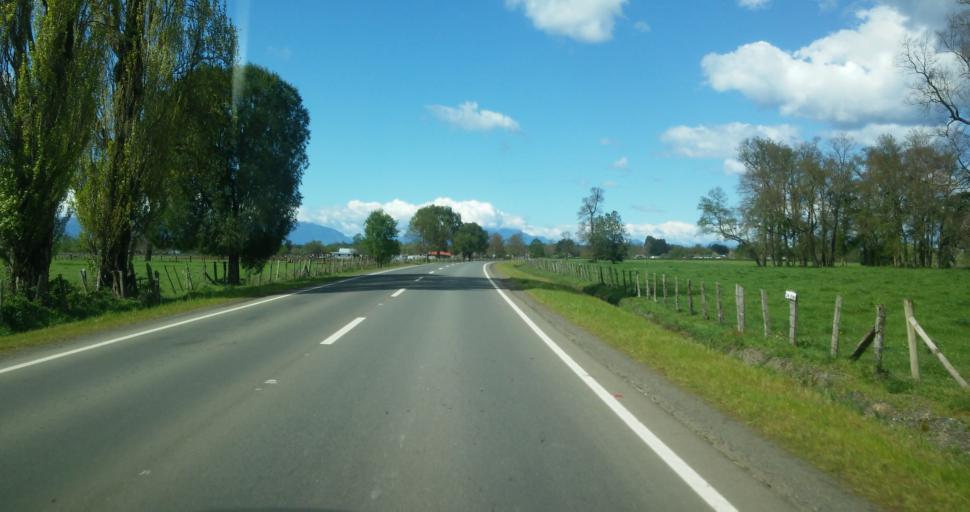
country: CL
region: Los Rios
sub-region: Provincia del Ranco
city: Rio Bueno
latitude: -40.2406
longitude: -72.6051
